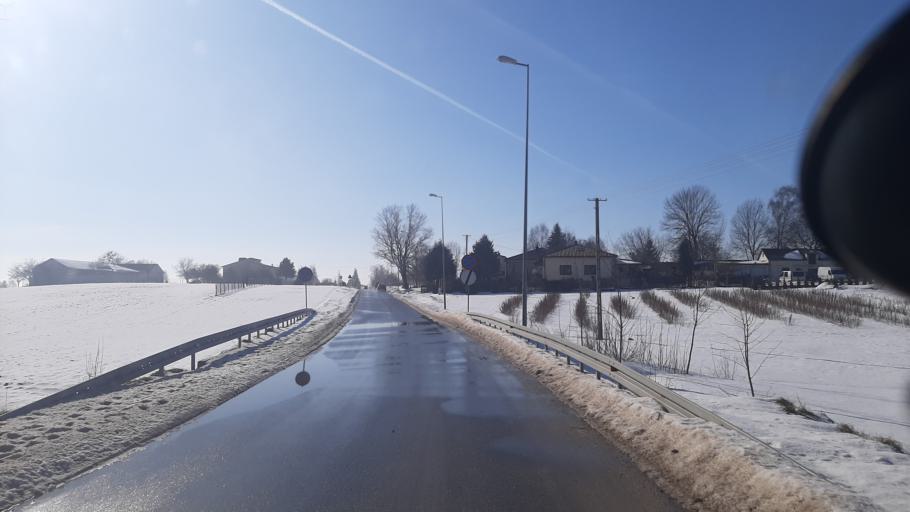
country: PL
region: Lublin Voivodeship
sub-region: Powiat lubelski
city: Garbow
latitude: 51.3119
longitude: 22.3077
